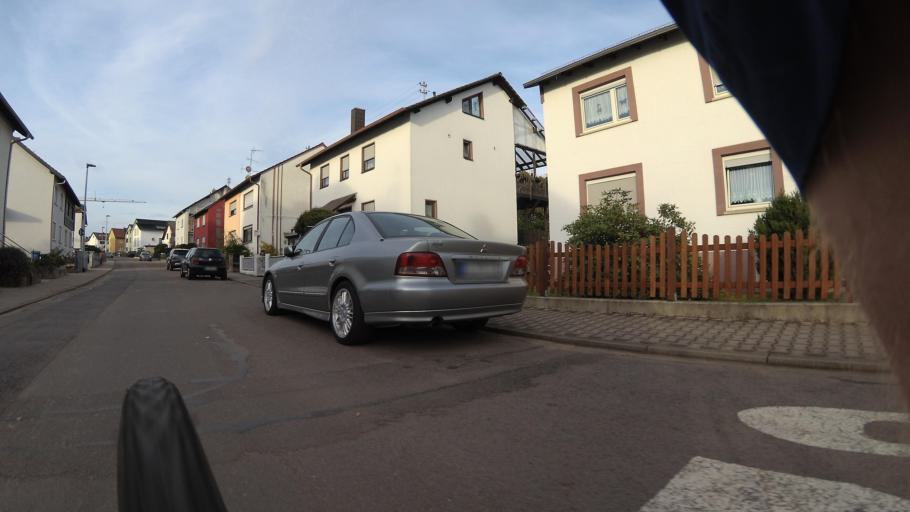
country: DE
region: Rheinland-Pfalz
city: Ramstein-Miesenbach
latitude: 49.4389
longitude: 7.5496
